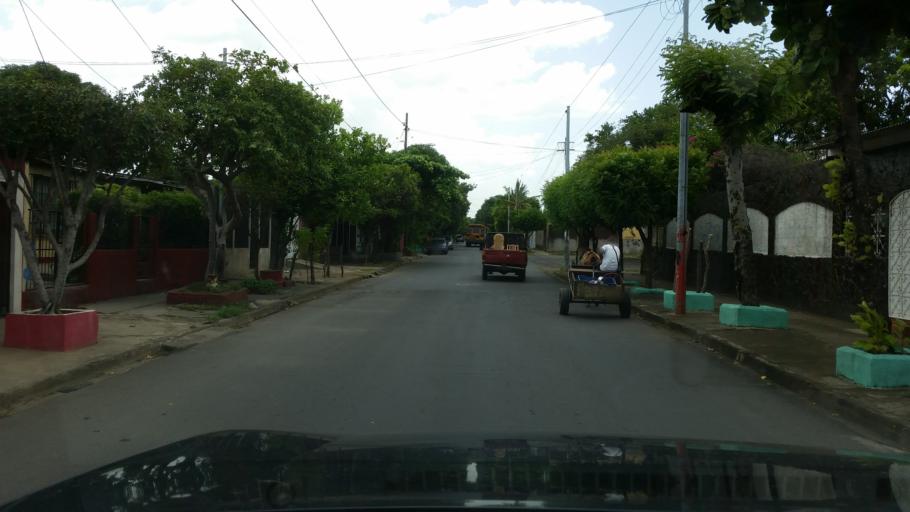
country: NI
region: Managua
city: Managua
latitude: 12.1219
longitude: -86.2196
